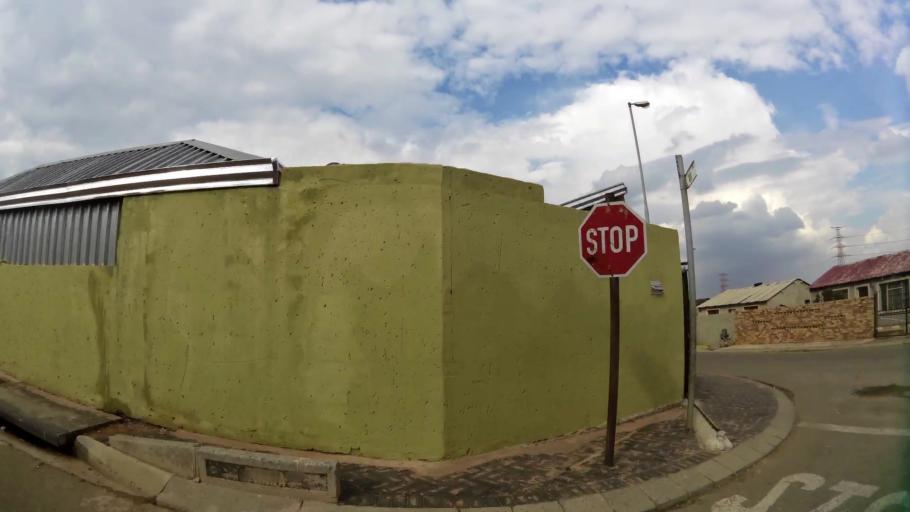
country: ZA
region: Gauteng
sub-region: City of Johannesburg Metropolitan Municipality
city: Soweto
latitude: -26.2363
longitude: 27.8701
